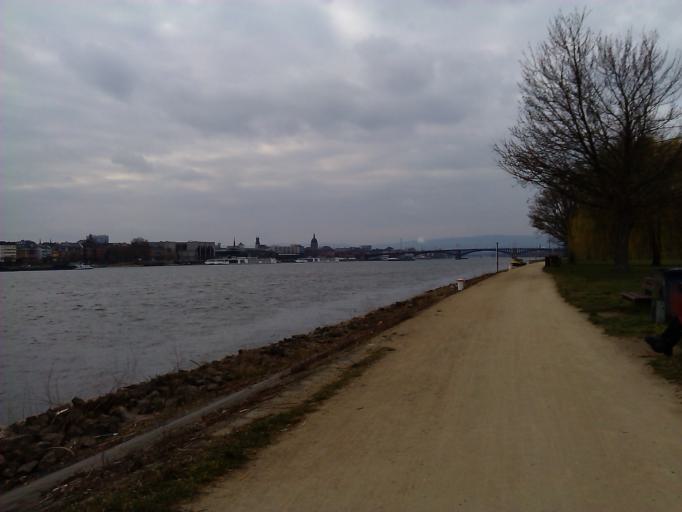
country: DE
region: Rheinland-Pfalz
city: Mainz
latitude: 49.9977
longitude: 8.2893
